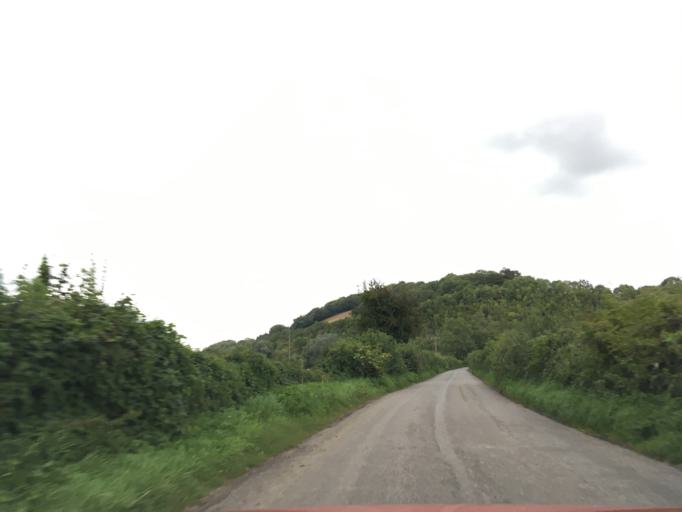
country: GB
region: Wales
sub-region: Monmouthshire
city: Llangybi
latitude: 51.6505
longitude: -2.8877
